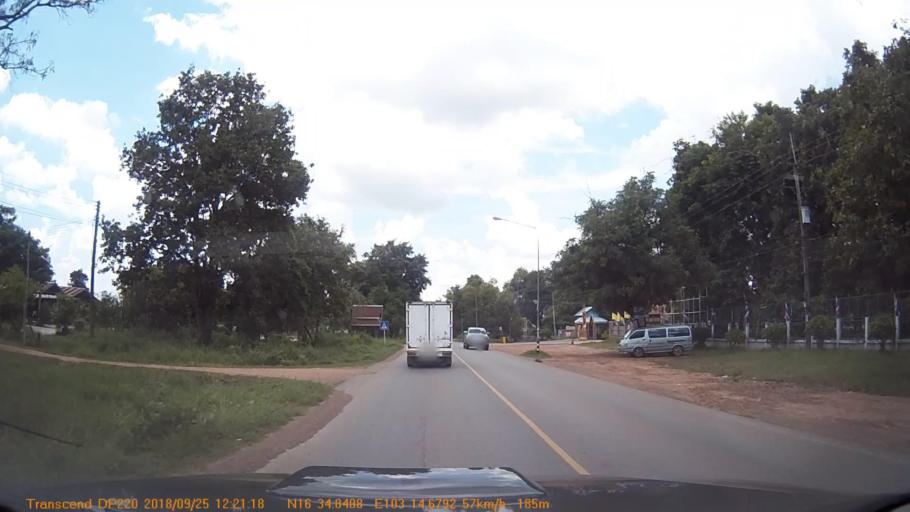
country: TH
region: Kalasin
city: Huai Mek
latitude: 16.5806
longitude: 103.2447
